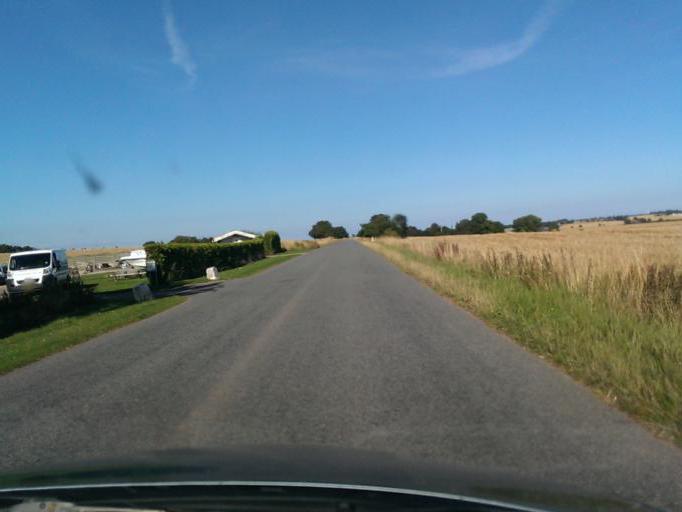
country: DK
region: Central Jutland
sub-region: Odder Kommune
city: Odder
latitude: 55.8992
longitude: 10.1293
